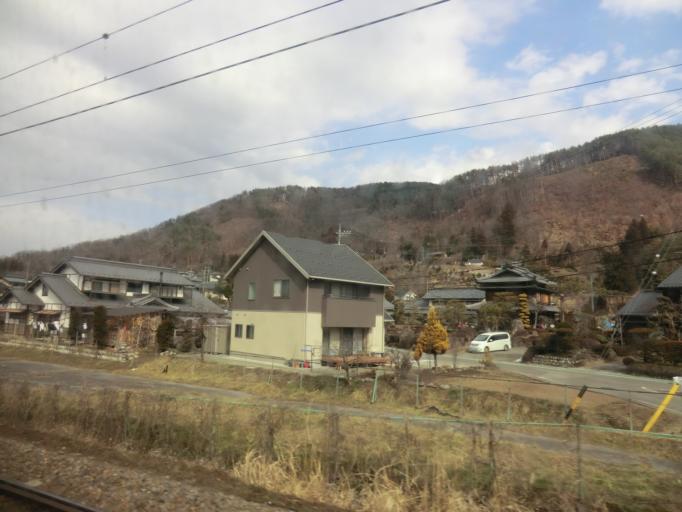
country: JP
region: Nagano
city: Hotaka
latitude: 36.3391
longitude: 137.9255
